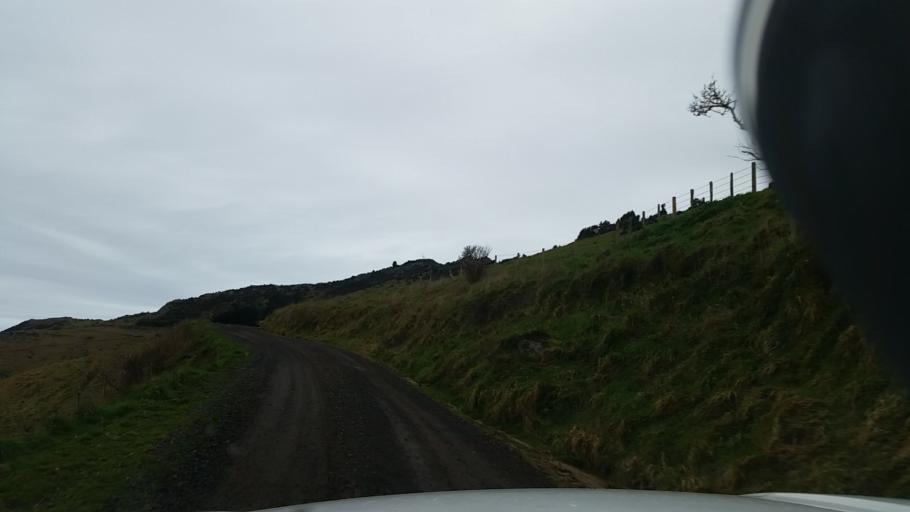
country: NZ
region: Canterbury
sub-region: Christchurch City
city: Christchurch
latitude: -43.7448
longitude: 173.0041
